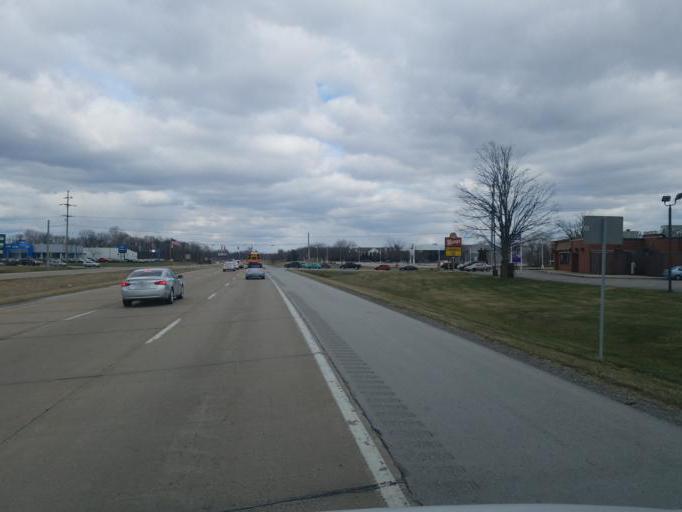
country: US
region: Indiana
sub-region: Hendricks County
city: Avon
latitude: 39.7587
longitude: -86.4349
